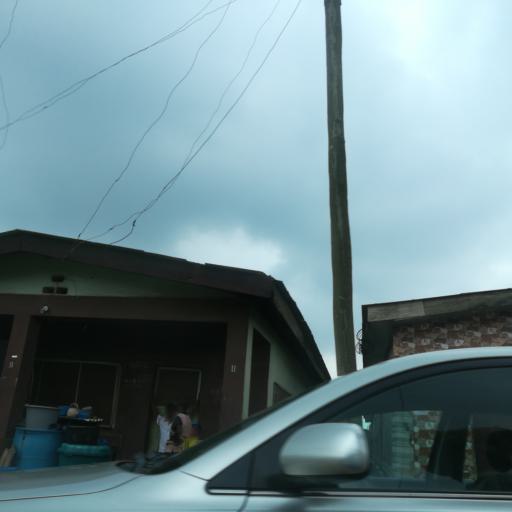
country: NG
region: Lagos
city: Agege
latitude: 6.5937
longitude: 3.2990
